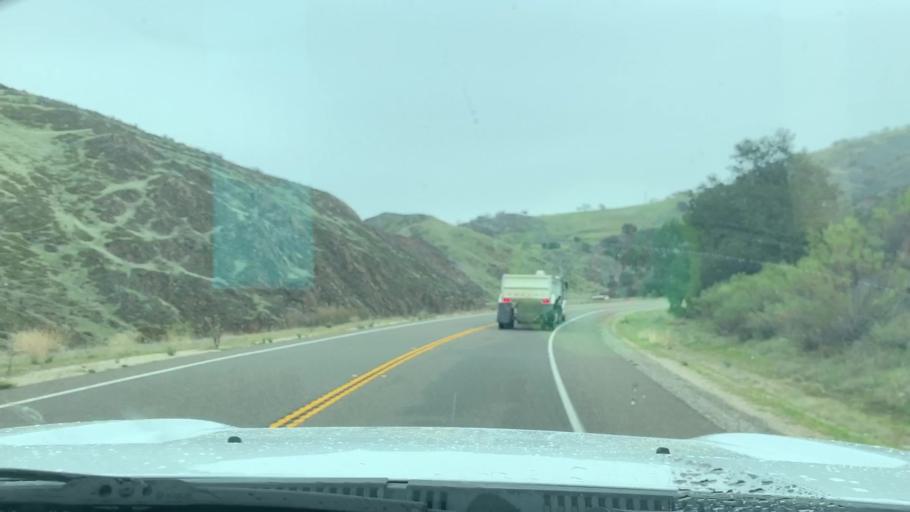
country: US
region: California
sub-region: Santa Barbara County
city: Santa Maria
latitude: 35.0613
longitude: -120.1773
